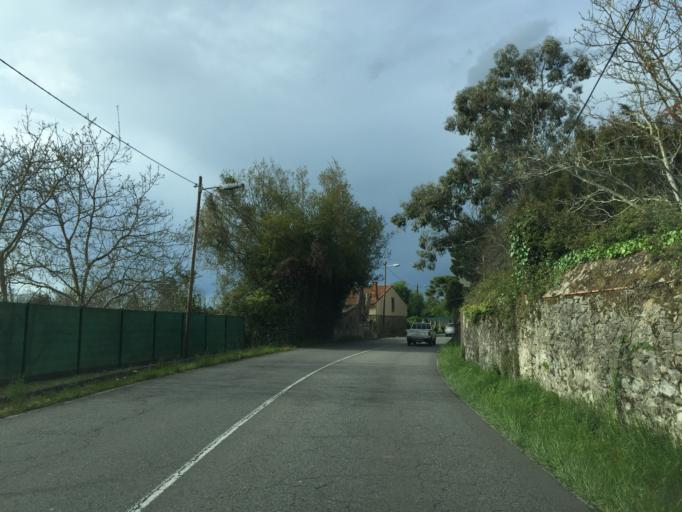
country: ES
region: Asturias
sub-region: Province of Asturias
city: Gijon
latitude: 43.5179
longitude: -5.6068
